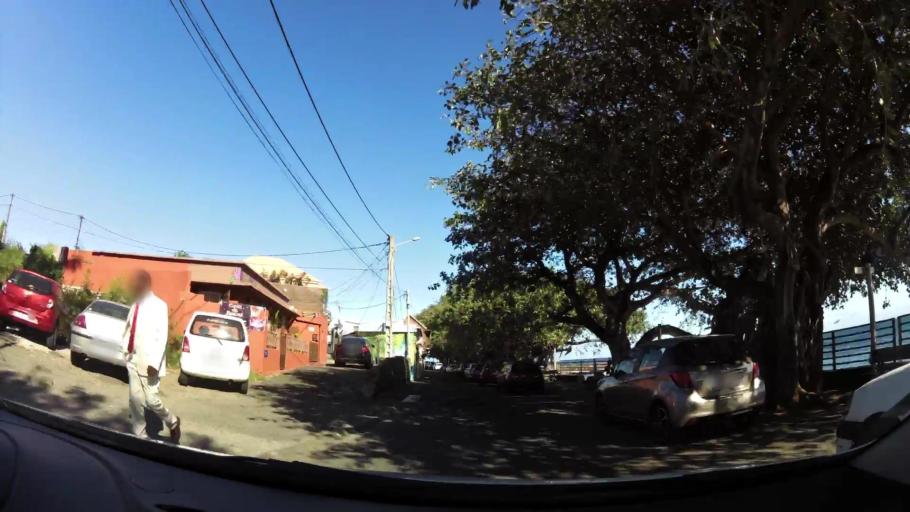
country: RE
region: Reunion
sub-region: Reunion
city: Saint-Pierre
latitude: -21.3457
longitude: 55.4805
